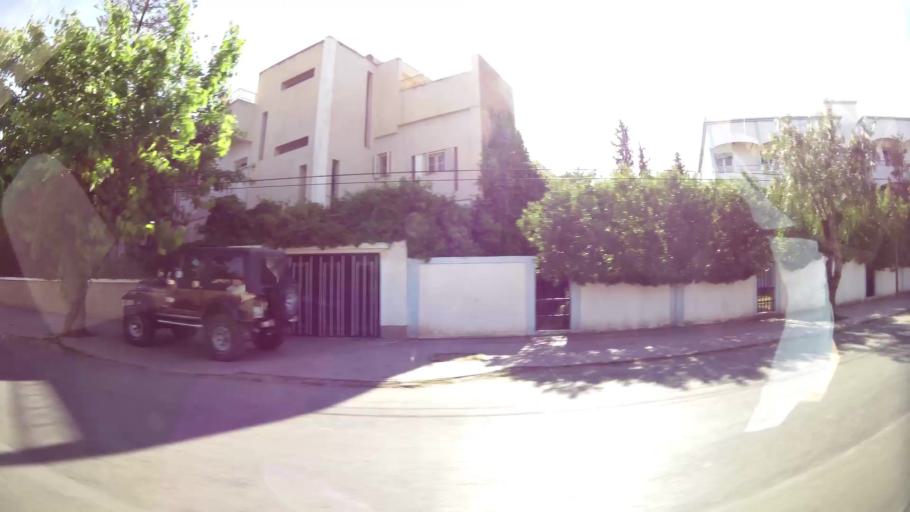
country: MA
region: Oriental
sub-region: Oujda-Angad
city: Oujda
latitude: 34.6694
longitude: -1.9107
